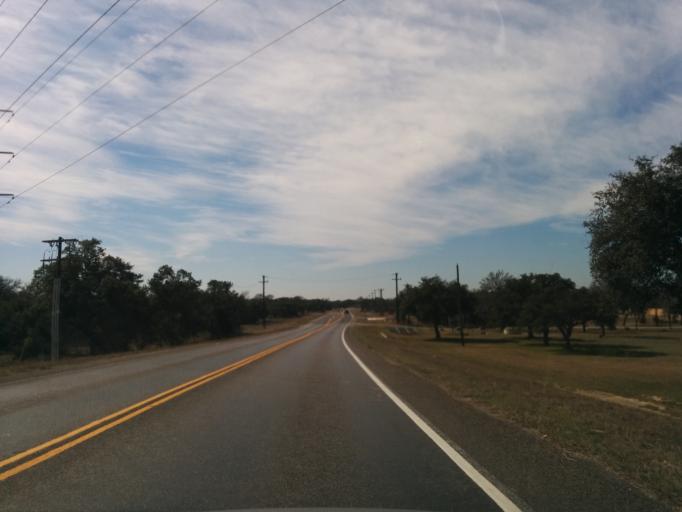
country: US
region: Texas
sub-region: Bexar County
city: Fair Oaks Ranch
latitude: 29.7621
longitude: -98.6116
